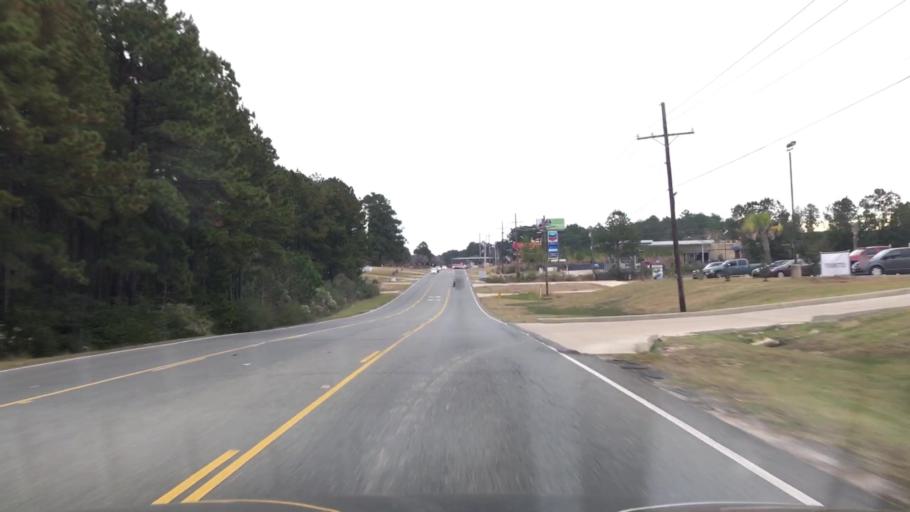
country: US
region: Louisiana
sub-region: Vernon Parish
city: Fort Polk South
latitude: 31.0544
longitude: -93.2394
